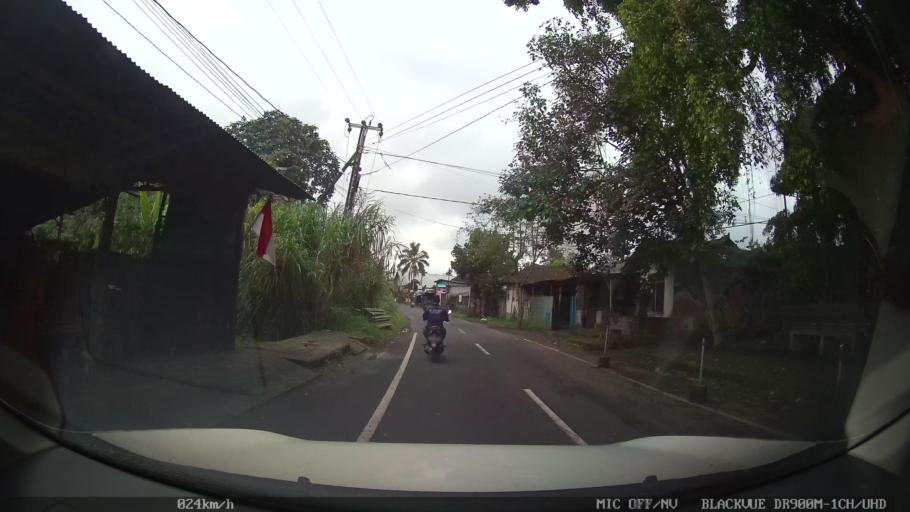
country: ID
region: Bali
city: Empalan
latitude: -8.3711
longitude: 115.1610
